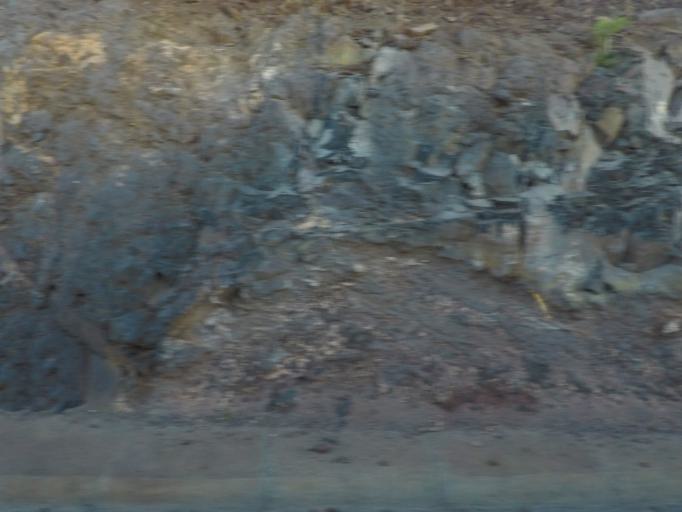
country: ES
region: Canary Islands
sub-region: Provincia de Santa Cruz de Tenerife
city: San Sebastian de la Gomera
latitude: 28.0885
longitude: -17.1240
